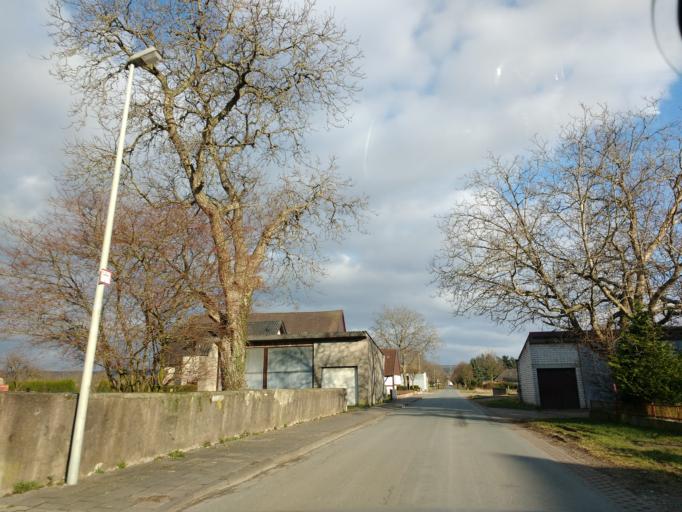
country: DE
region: North Rhine-Westphalia
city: Bad Lippspringe
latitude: 51.7789
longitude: 8.8294
